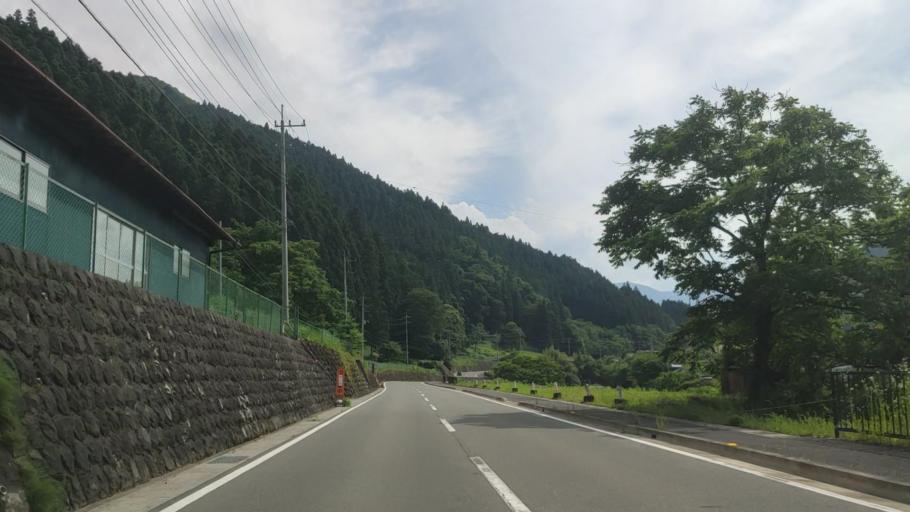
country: JP
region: Gunma
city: Tomioka
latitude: 36.1733
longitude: 138.7363
